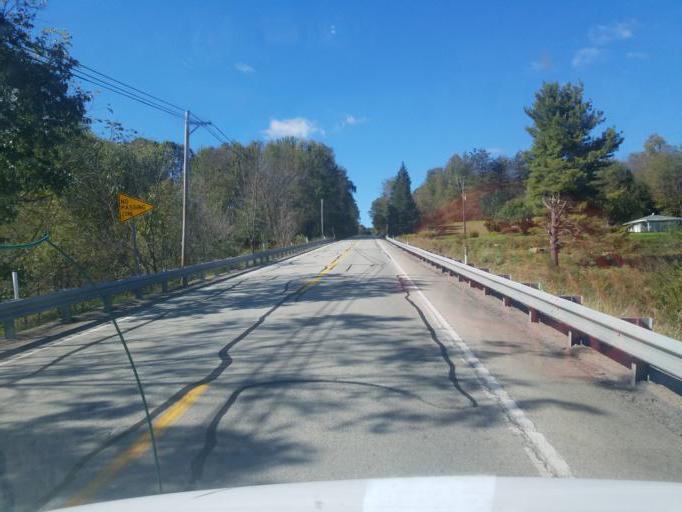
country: US
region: Pennsylvania
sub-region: Somerset County
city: Boswell
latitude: 40.1675
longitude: -79.0971
